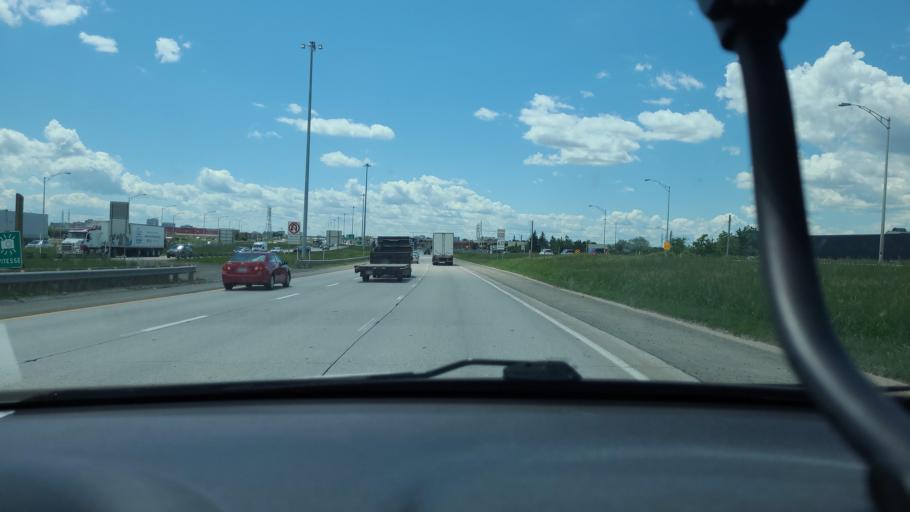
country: CA
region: Quebec
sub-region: Laval
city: Laval
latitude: 45.5876
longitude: -73.7321
